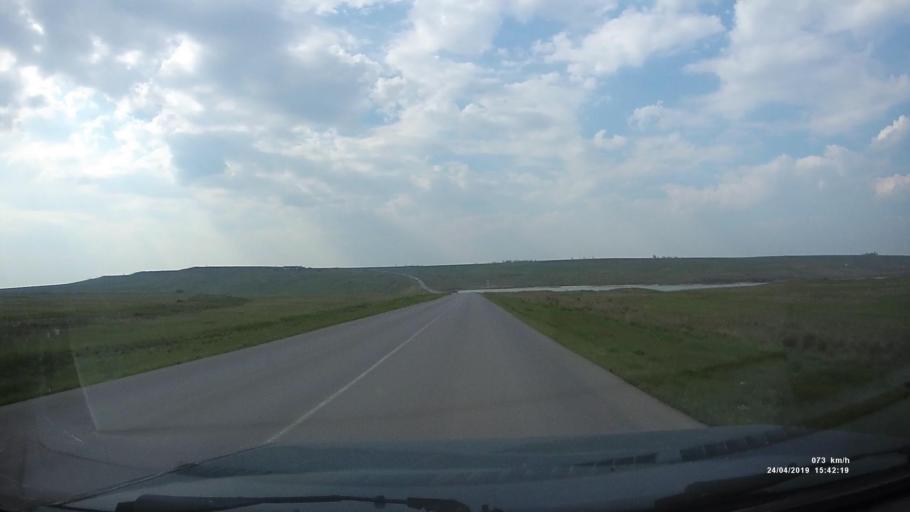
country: RU
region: Kalmykiya
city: Yashalta
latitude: 46.5750
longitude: 42.7895
